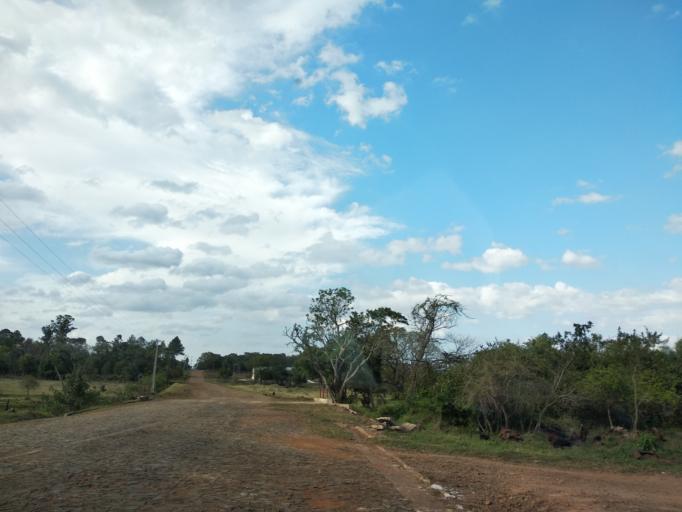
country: PY
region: Itapua
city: San Juan del Parana
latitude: -27.3050
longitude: -55.9602
